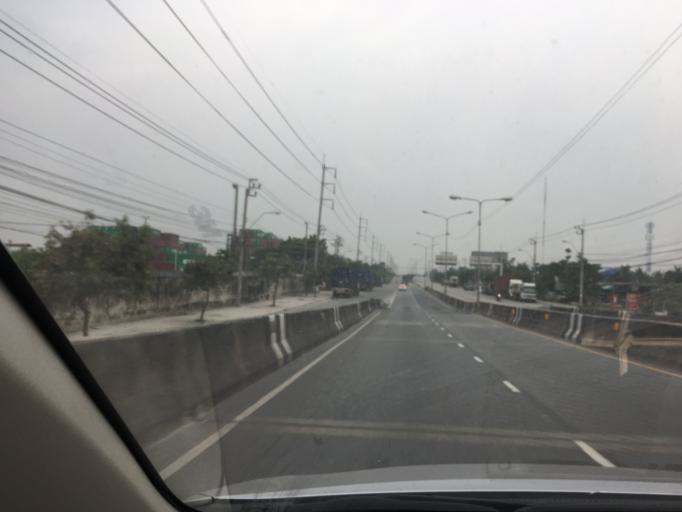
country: TH
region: Bangkok
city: Lat Krabang
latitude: 13.7546
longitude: 100.7596
